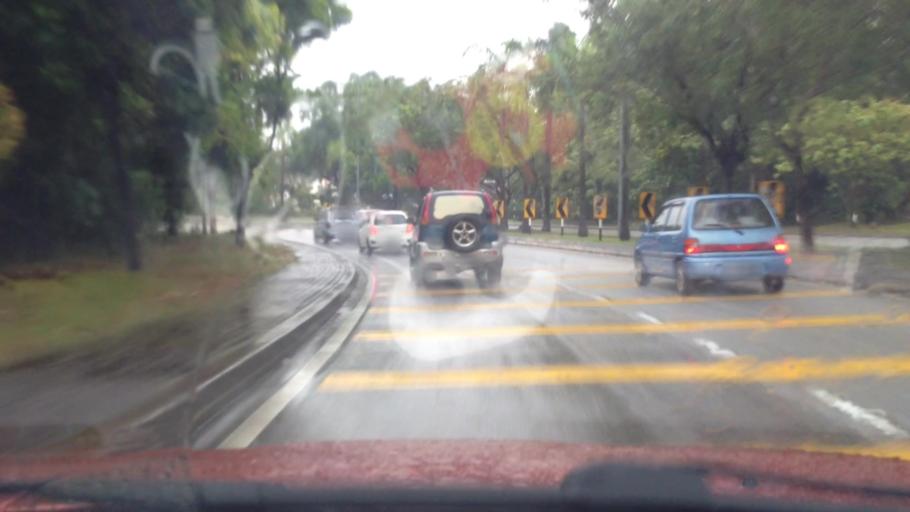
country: MY
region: Selangor
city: Subang Jaya
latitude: 3.0584
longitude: 101.5716
